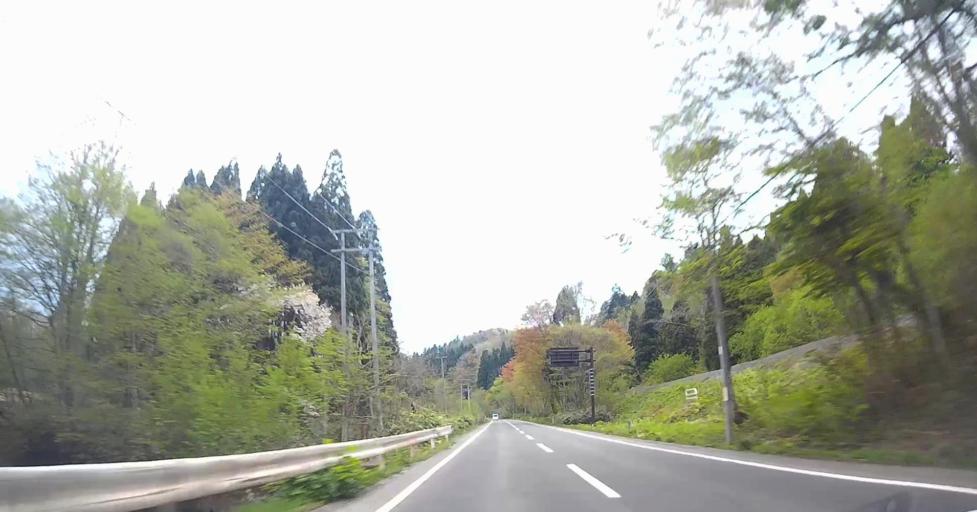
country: JP
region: Aomori
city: Goshogawara
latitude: 41.1274
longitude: 140.5197
